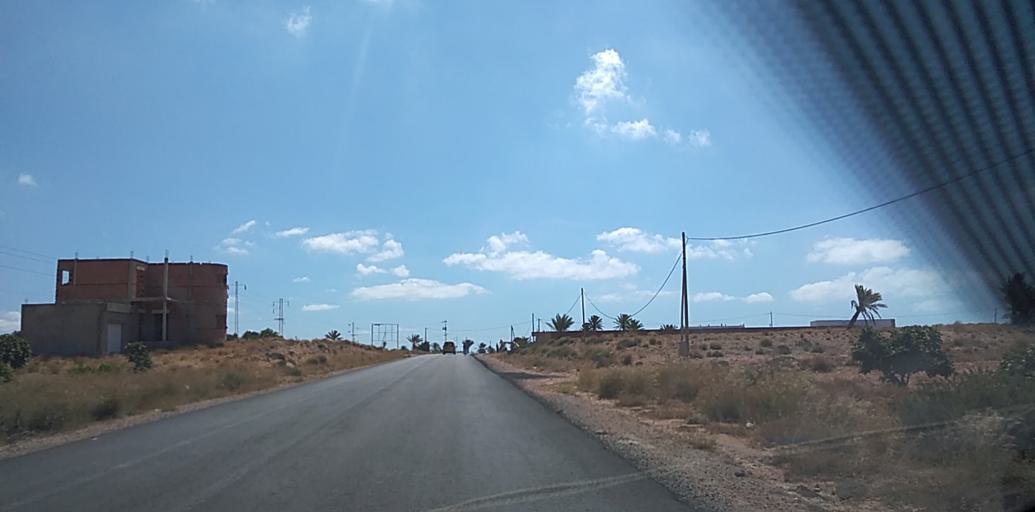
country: TN
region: Safaqis
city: Al Qarmadah
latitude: 34.6575
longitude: 11.0799
